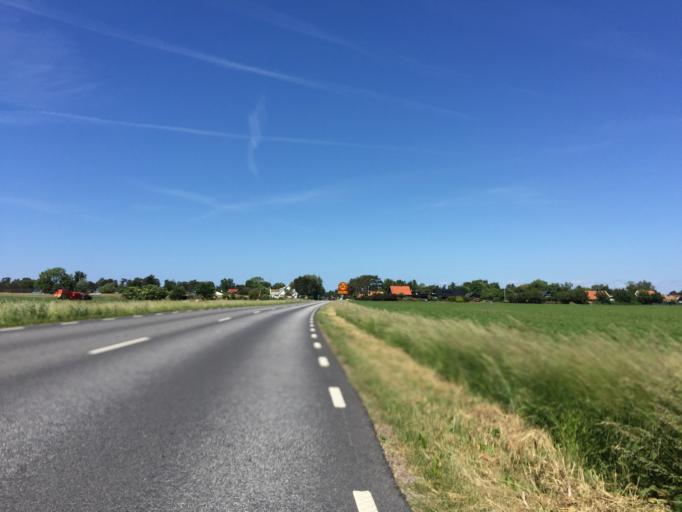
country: SE
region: Skane
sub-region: Vellinge Kommun
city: Hollviken
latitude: 55.3986
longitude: 12.9865
